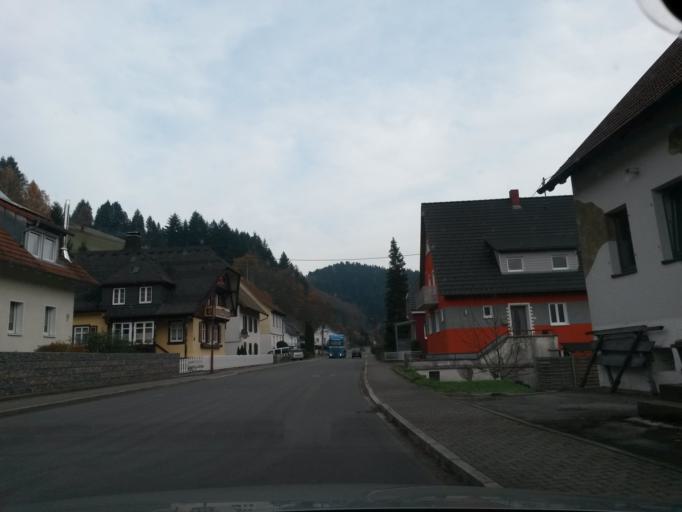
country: DE
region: Baden-Wuerttemberg
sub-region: Freiburg Region
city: Schenkenzell
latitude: 48.3120
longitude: 8.3733
